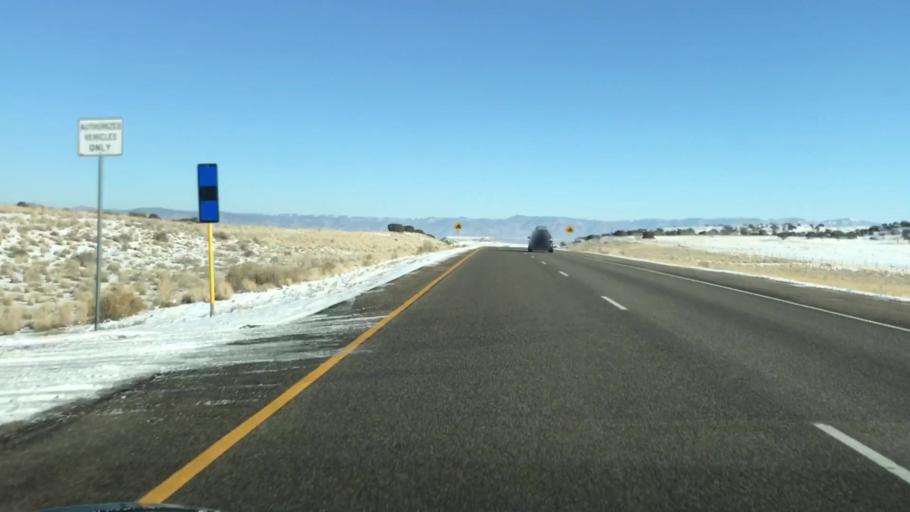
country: US
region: Colorado
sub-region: Mesa County
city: Loma
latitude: 39.2141
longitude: -108.9643
